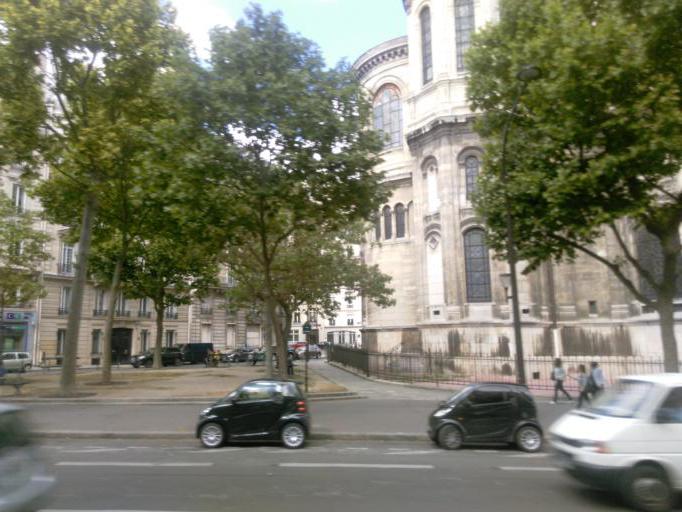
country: FR
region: Ile-de-France
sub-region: Departement des Hauts-de-Seine
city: Clichy
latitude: 48.8765
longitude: 2.3183
